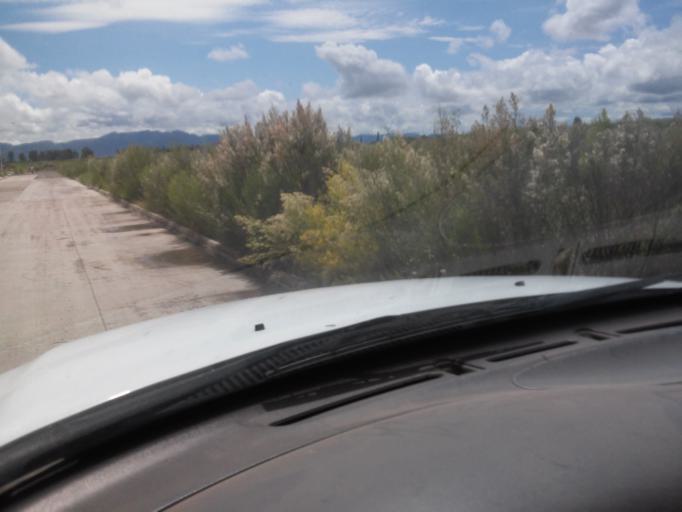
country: MX
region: Durango
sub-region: Durango
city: Jose Refugio Salcido
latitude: 24.0152
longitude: -104.5460
